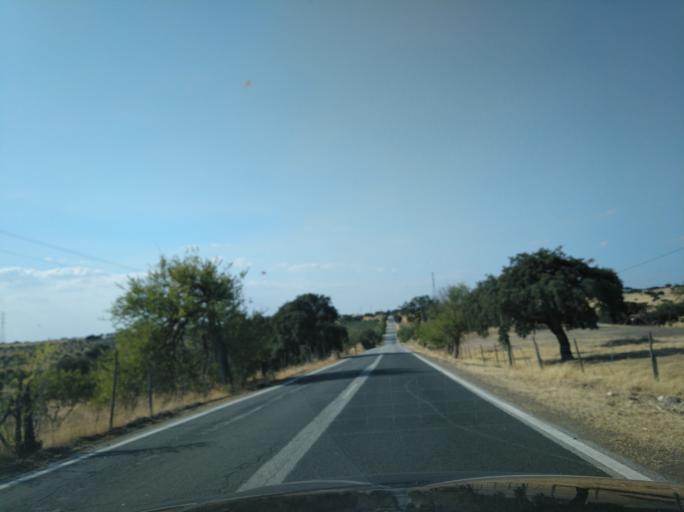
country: ES
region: Extremadura
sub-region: Provincia de Badajoz
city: Valencia del Mombuey
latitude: 38.2366
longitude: -7.2365
